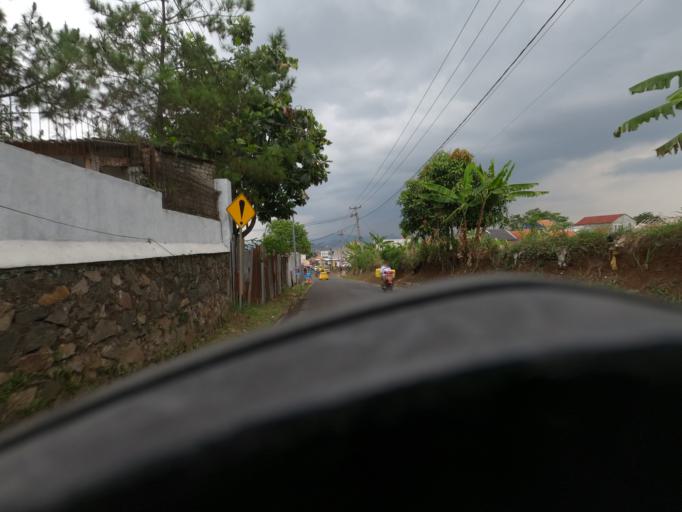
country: ID
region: West Java
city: Padalarang
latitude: -6.8393
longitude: 107.5087
